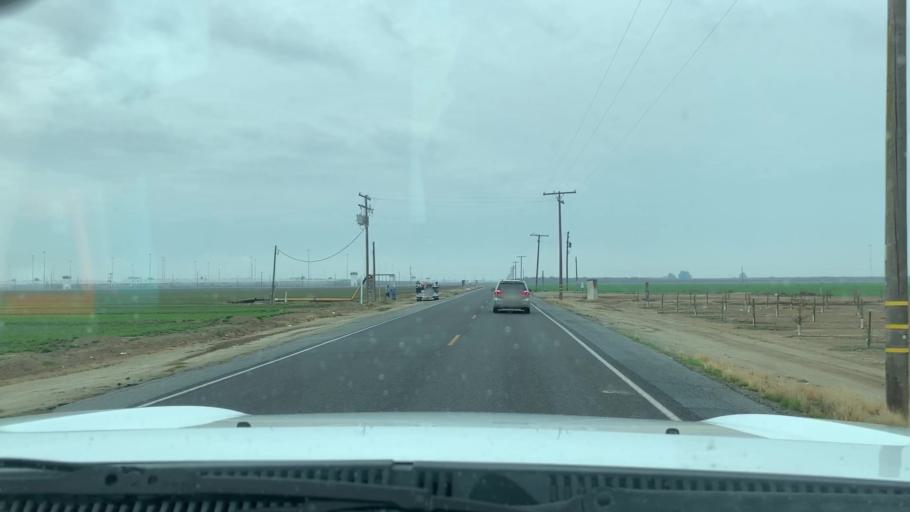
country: US
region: California
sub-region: Kern County
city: Delano
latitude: 35.7612
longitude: -119.3351
